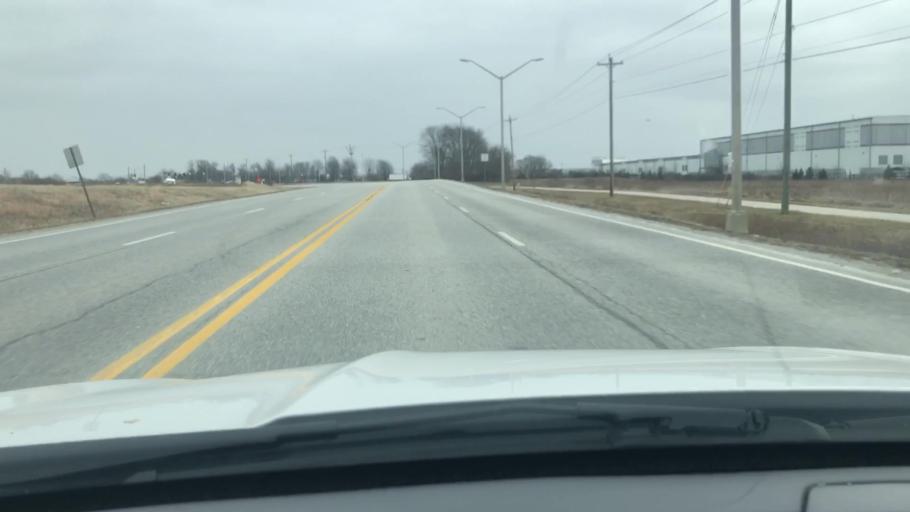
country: US
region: Indiana
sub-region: Tippecanoe County
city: Dayton
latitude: 40.3673
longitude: -86.8298
